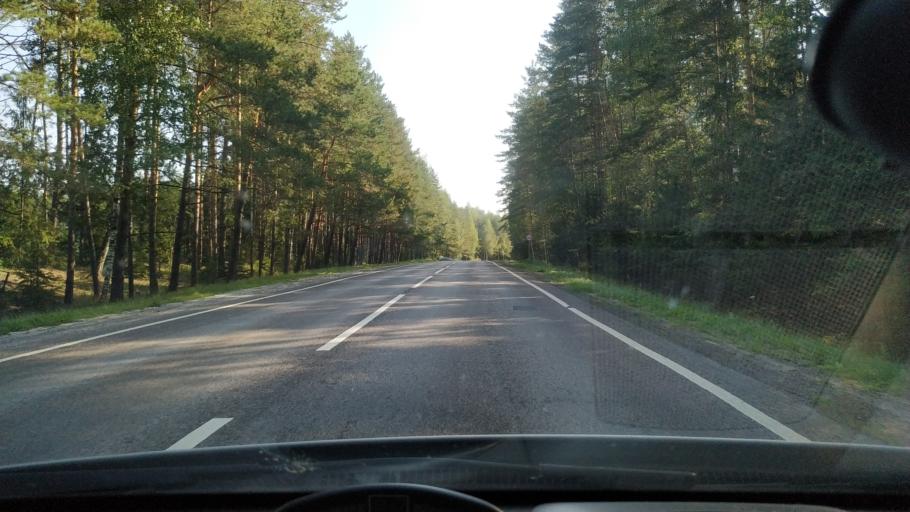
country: RU
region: Moskovskaya
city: Dmitrovskiy Pogost
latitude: 55.2350
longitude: 39.9586
